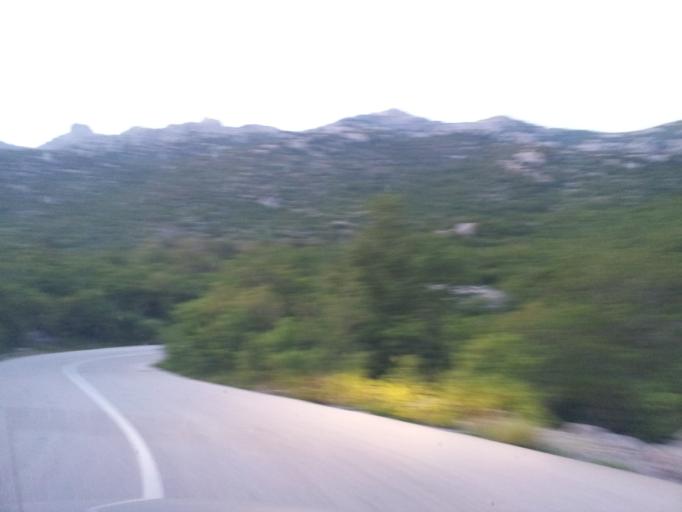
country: HR
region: Zadarska
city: Obrovac
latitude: 44.2422
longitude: 15.6651
